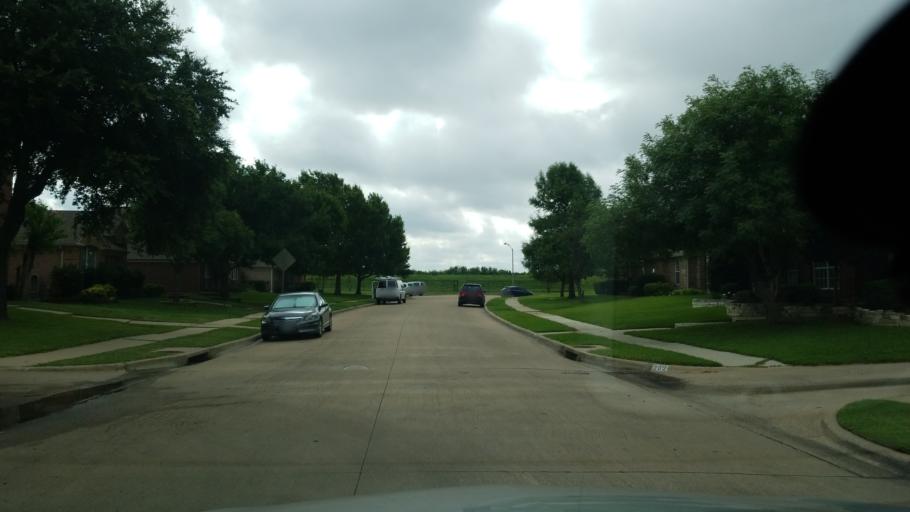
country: US
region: Texas
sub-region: Dallas County
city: Farmers Branch
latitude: 32.9416
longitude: -96.9442
